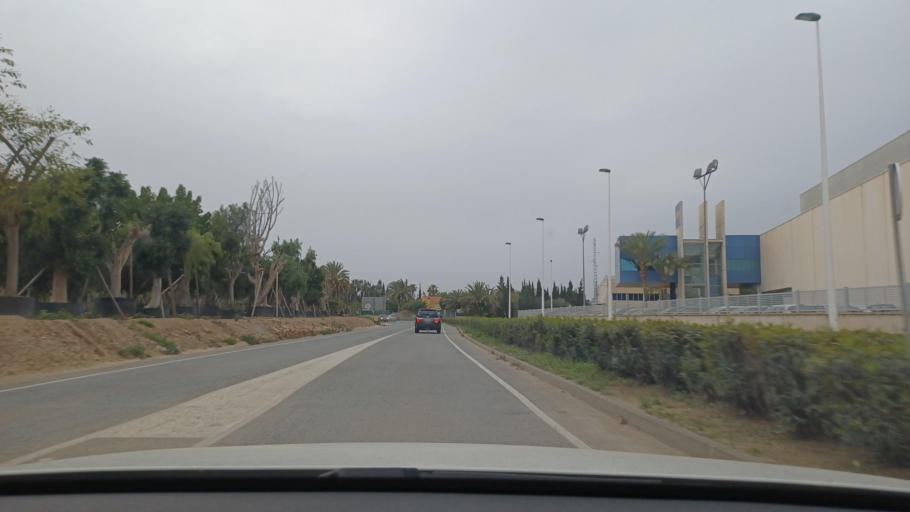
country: ES
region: Valencia
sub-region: Provincia de Alicante
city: Elche
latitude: 38.2421
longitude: -0.6861
